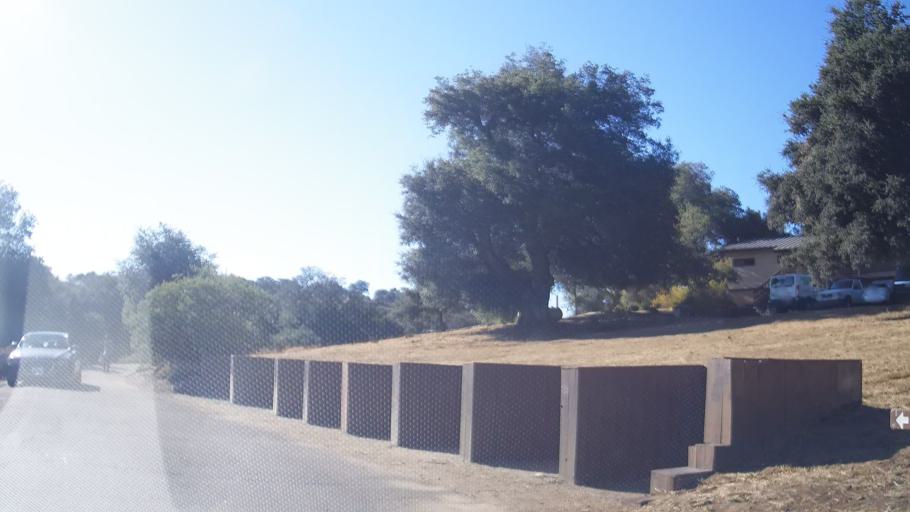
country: US
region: California
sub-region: San Diego County
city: Julian
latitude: 33.0389
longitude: -116.6384
